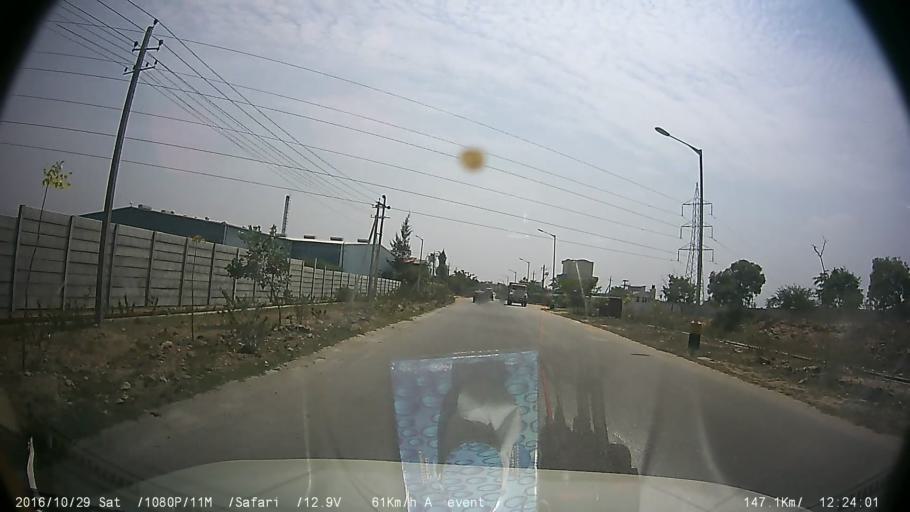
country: IN
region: Karnataka
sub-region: Mysore
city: Mysore
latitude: 12.3562
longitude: 76.5637
